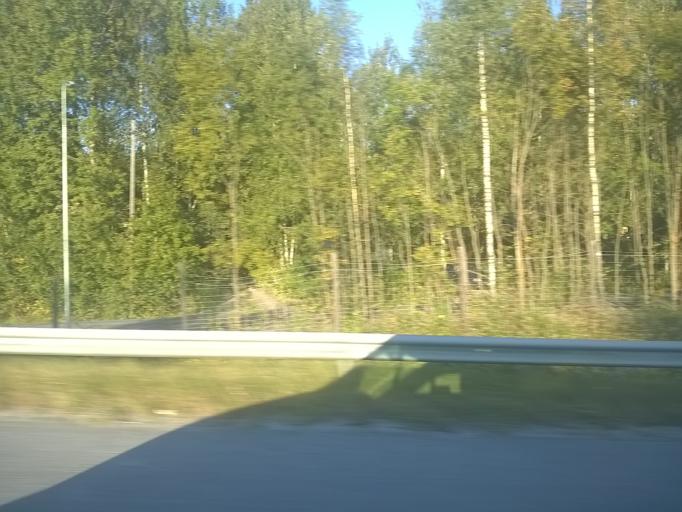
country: FI
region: Pirkanmaa
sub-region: Tampere
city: Tampere
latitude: 61.4254
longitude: 23.7549
